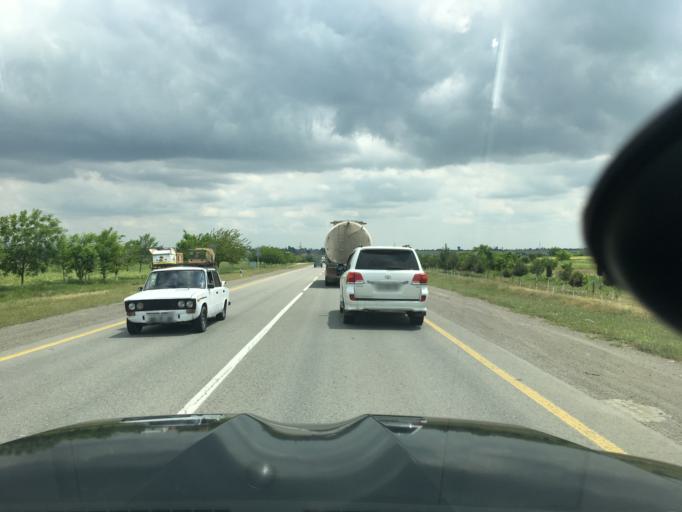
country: AZ
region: Tovuz
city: Qaraxanli
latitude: 41.0293
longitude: 45.6045
